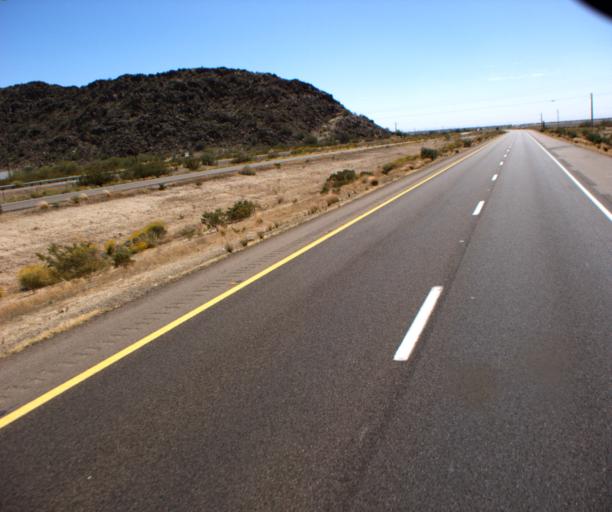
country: US
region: Arizona
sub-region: Maricopa County
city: Buckeye
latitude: 33.1759
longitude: -112.6508
